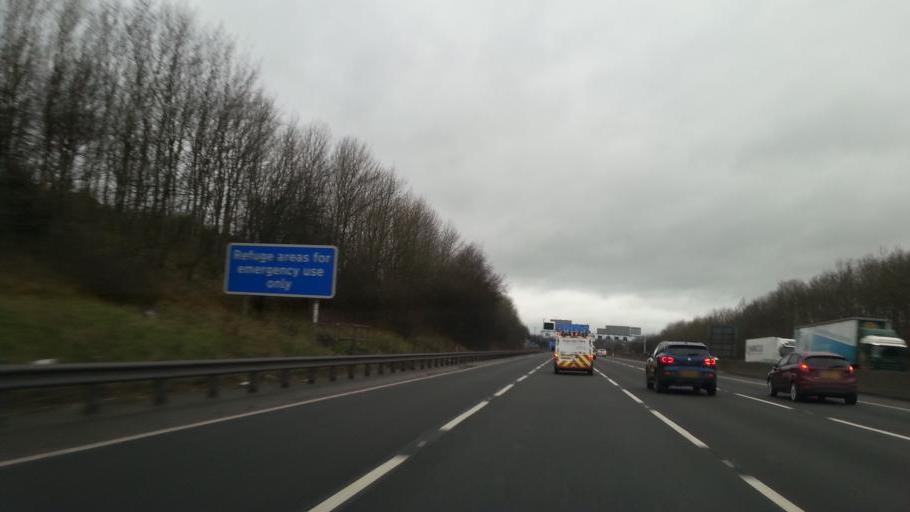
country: GB
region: England
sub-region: City and Borough of Leeds
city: Lofthouse
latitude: 53.7282
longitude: -1.4698
